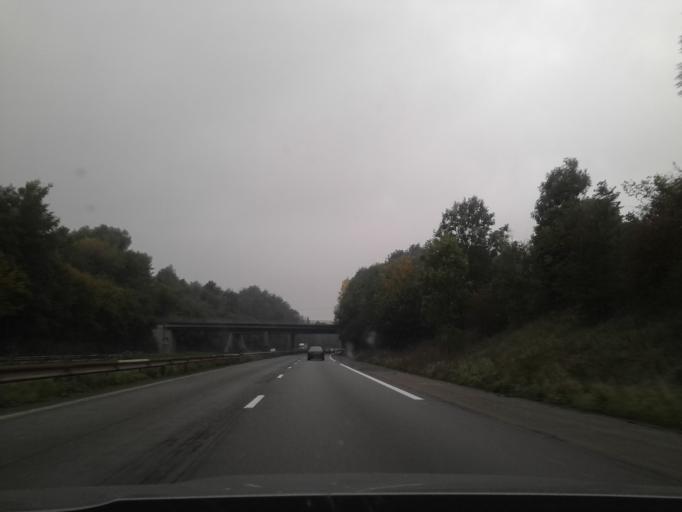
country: FR
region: Nord-Pas-de-Calais
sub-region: Departement du Nord
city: Saultain
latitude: 50.3422
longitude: 3.5681
